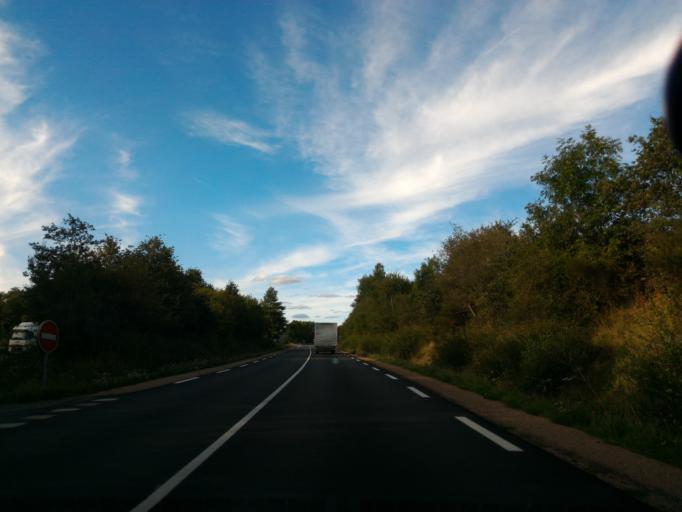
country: FR
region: Limousin
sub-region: Departement de la Haute-Vienne
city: Magnac-Laval
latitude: 46.1600
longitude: 1.1325
